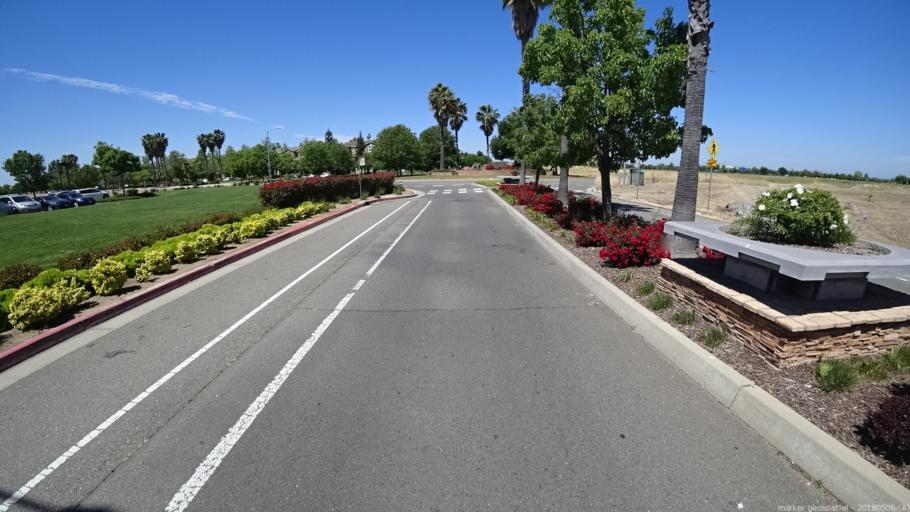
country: US
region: California
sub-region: Yolo County
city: West Sacramento
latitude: 38.6576
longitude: -121.5221
